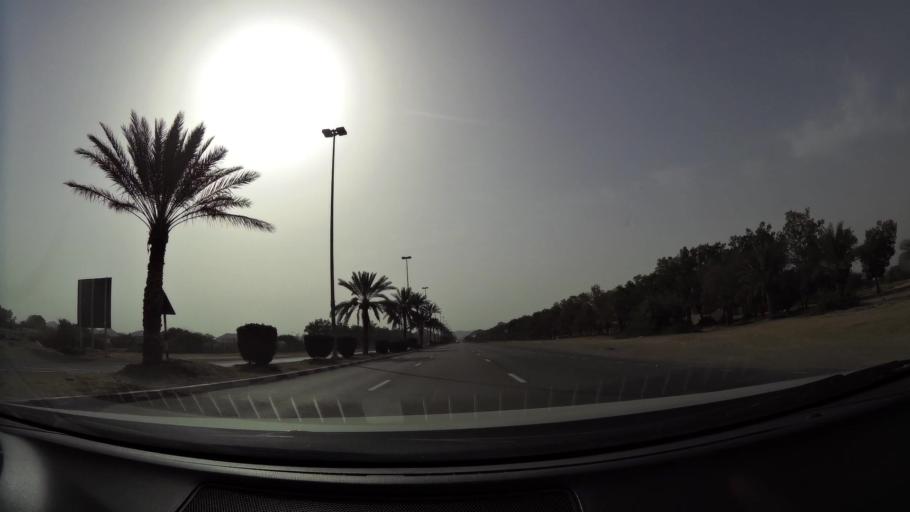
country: AE
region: Abu Dhabi
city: Al Ain
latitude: 24.1355
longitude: 55.7156
